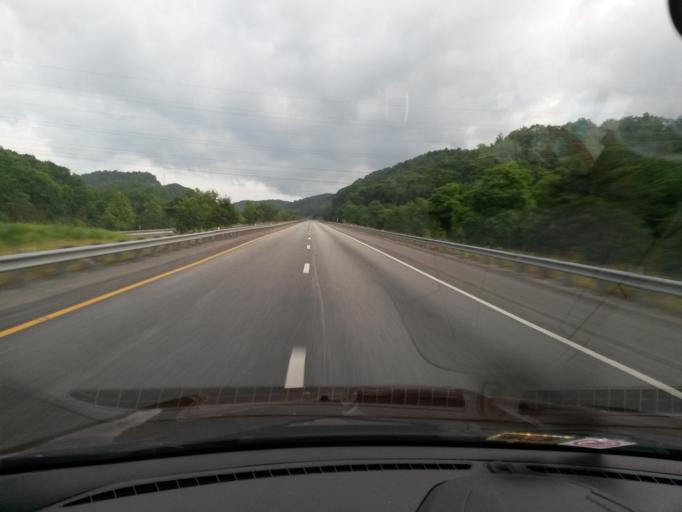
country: US
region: Virginia
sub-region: City of Covington
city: Covington
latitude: 37.7804
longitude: -80.0059
